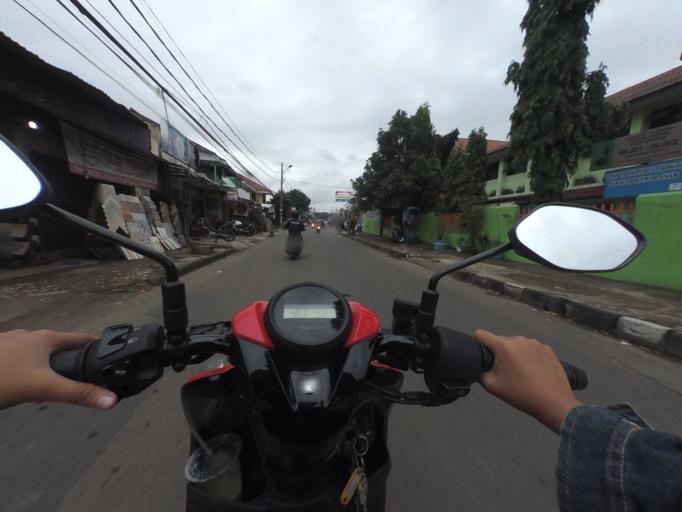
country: ID
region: West Java
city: Bogor
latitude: -6.5653
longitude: 106.8019
